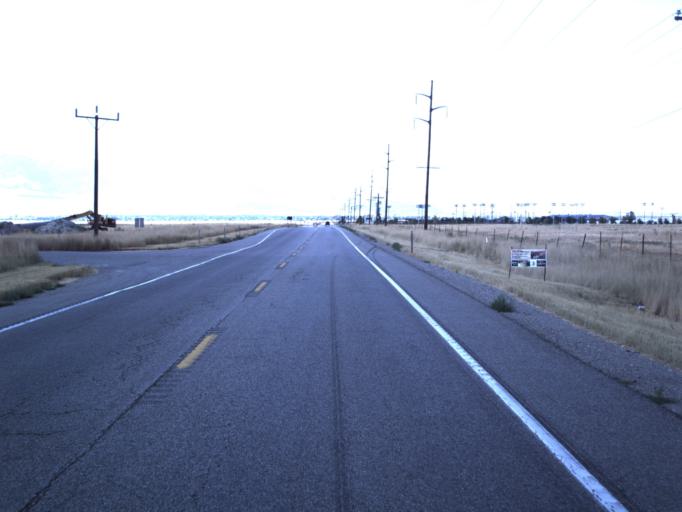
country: US
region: Utah
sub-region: Tooele County
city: Tooele
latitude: 40.5647
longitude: -112.3625
